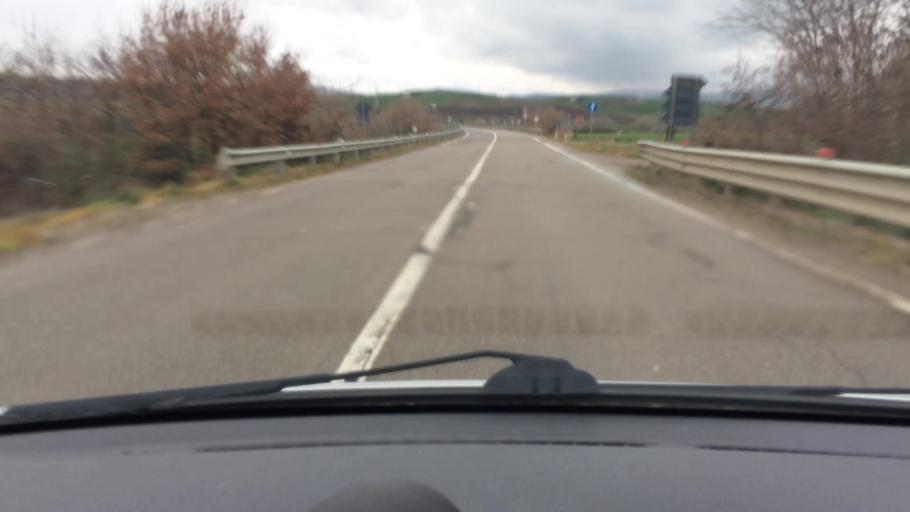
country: IT
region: Basilicate
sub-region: Provincia di Potenza
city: San Chirico Nuovo
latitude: 40.7710
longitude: 16.1149
